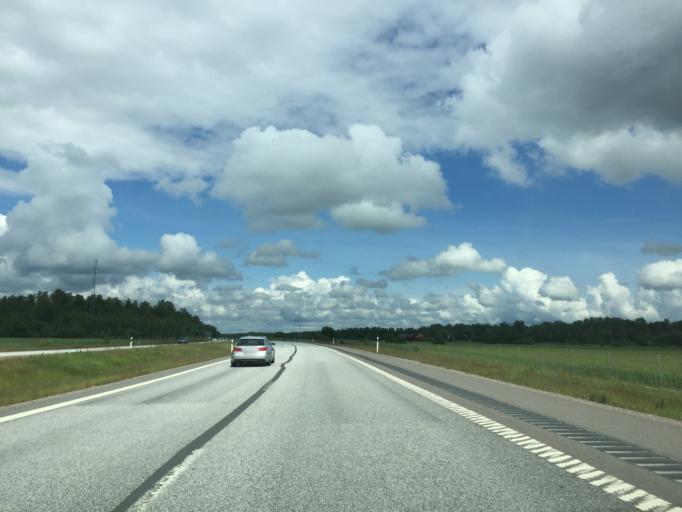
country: SE
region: Vaestmanland
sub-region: Arboga Kommun
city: Arboga
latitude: 59.4422
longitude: 15.9007
